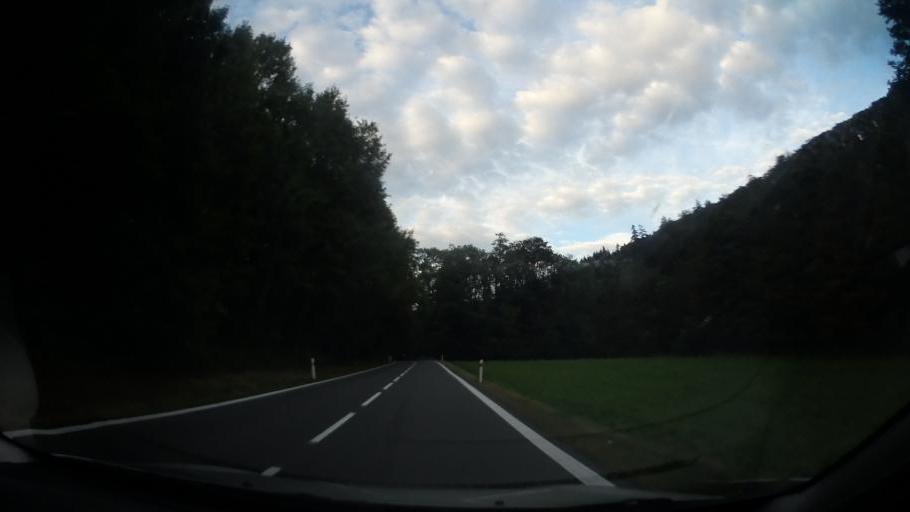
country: CZ
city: Rymarov
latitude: 49.8913
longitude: 17.2577
